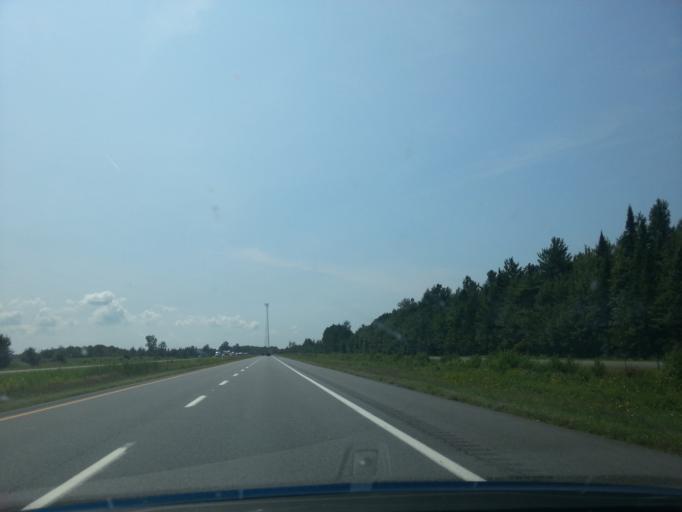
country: CA
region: Quebec
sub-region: Mauricie
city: Daveluyville
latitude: 46.2492
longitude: -72.0488
